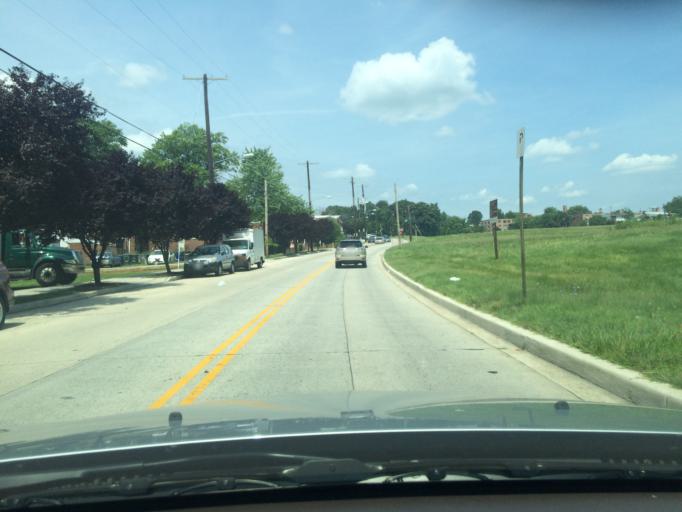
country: US
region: Maryland
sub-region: Prince George's County
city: Chillum
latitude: 38.9513
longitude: -76.9858
